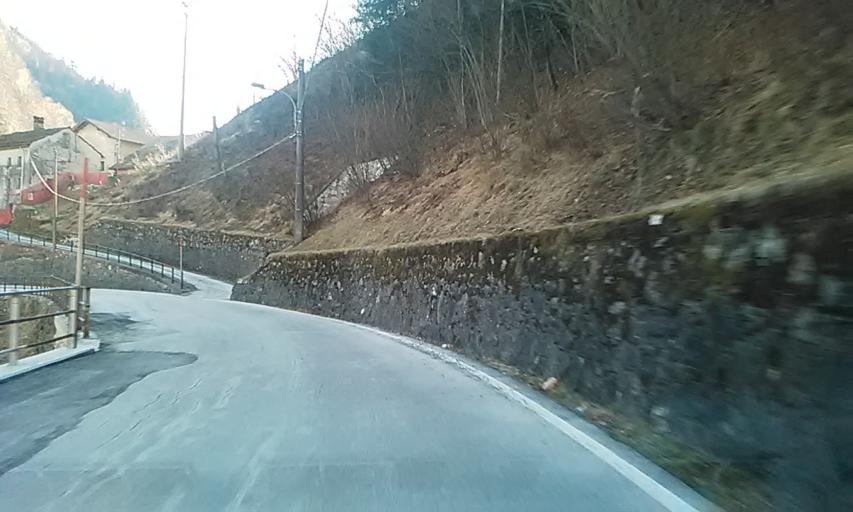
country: IT
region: Piedmont
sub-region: Provincia di Vercelli
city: Rimasco
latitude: 45.8557
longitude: 8.0631
